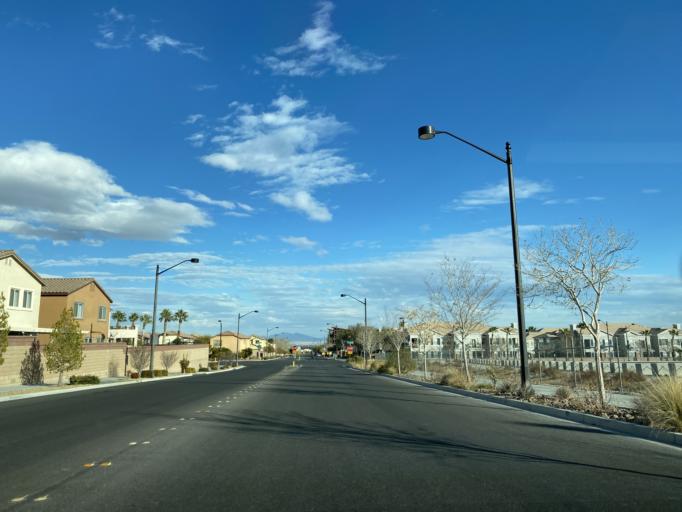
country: US
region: Nevada
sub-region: Clark County
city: Summerlin South
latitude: 36.2827
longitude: -115.2981
